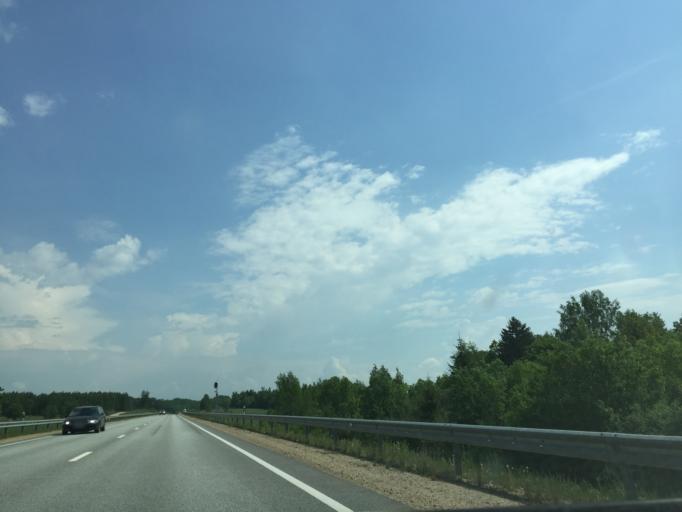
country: LV
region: Ogre
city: Jumprava
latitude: 56.7756
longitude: 25.0541
